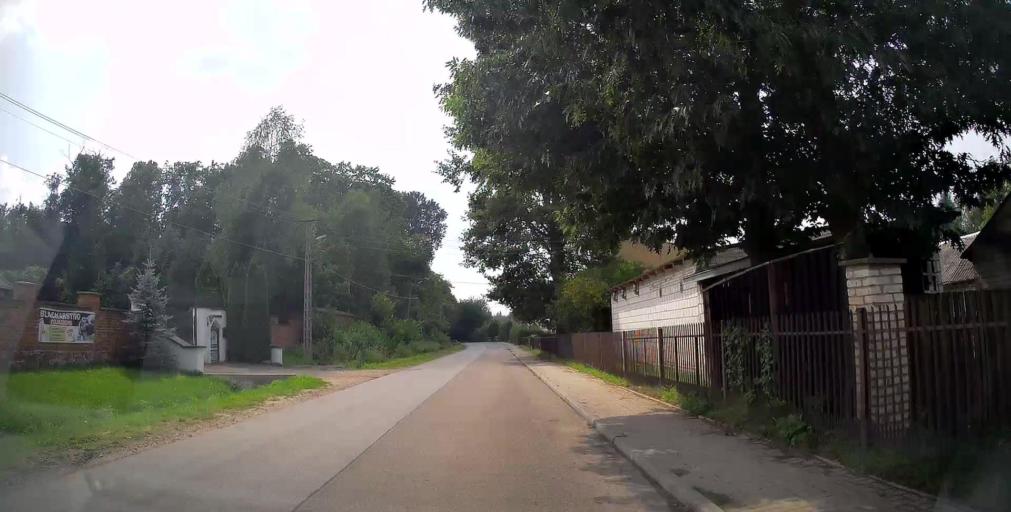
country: PL
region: Masovian Voivodeship
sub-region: Powiat bialobrzeski
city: Sucha
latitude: 51.6225
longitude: 20.9521
